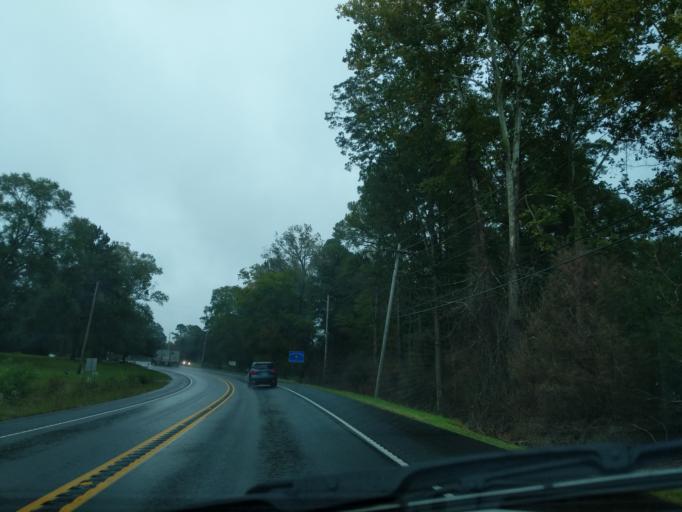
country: US
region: Louisiana
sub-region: Caddo Parish
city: Greenwood
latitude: 32.3738
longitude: -94.0363
